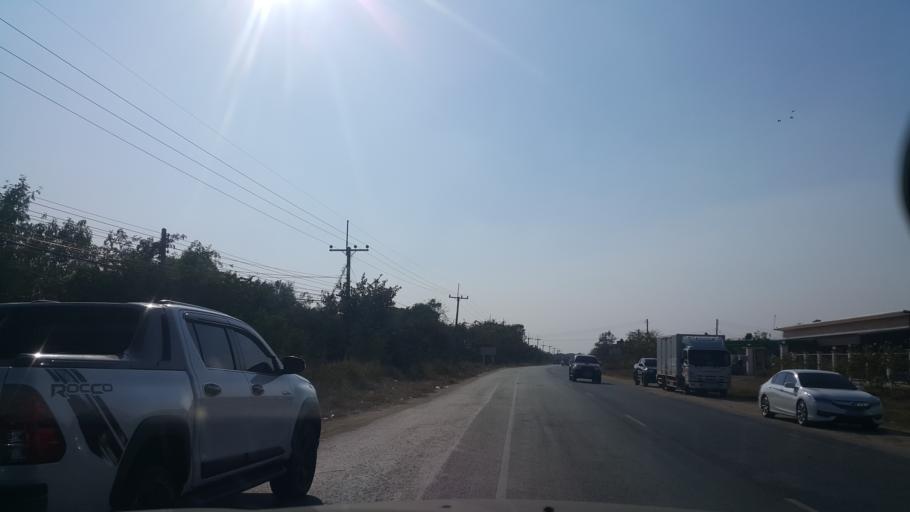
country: TH
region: Nakhon Ratchasima
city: Phimai
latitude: 15.2135
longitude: 102.4792
